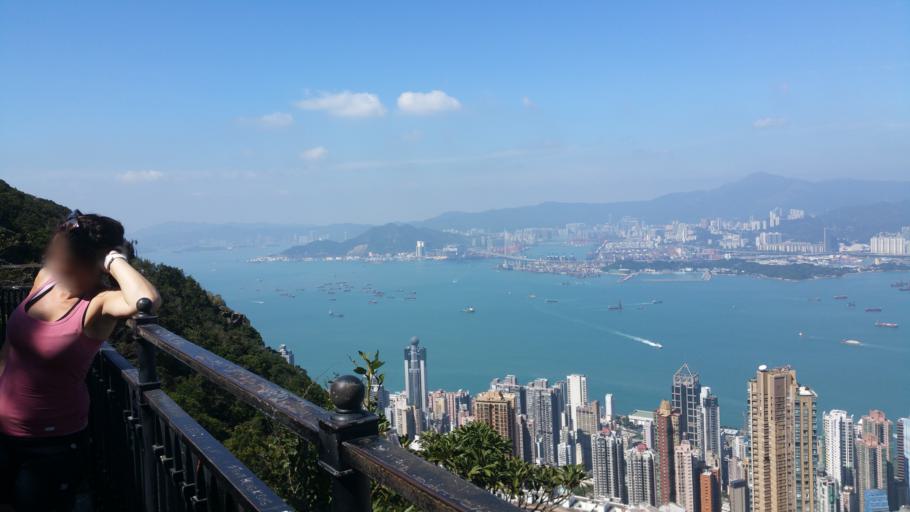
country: HK
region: Central and Western
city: Central
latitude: 22.2777
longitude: 114.1476
